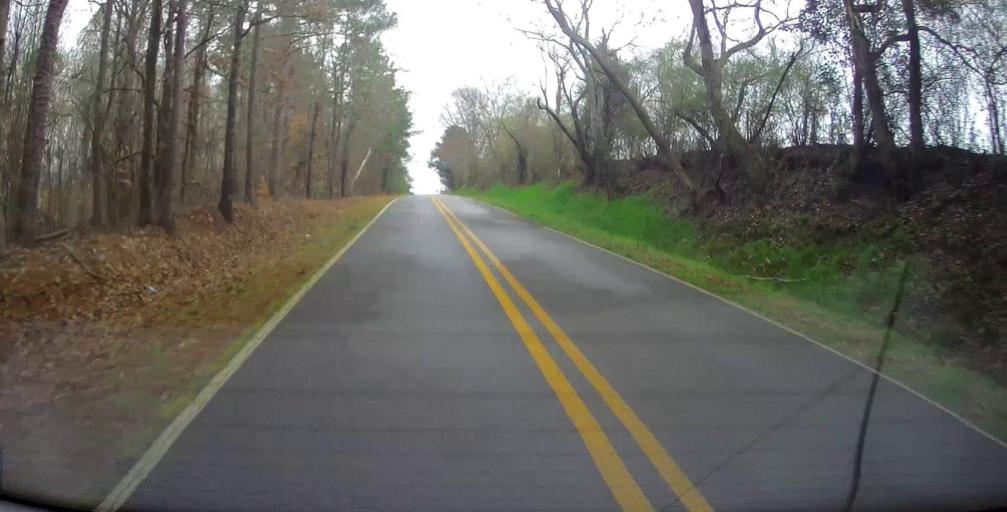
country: US
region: Georgia
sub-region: Monroe County
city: Forsyth
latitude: 33.0319
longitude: -83.8690
